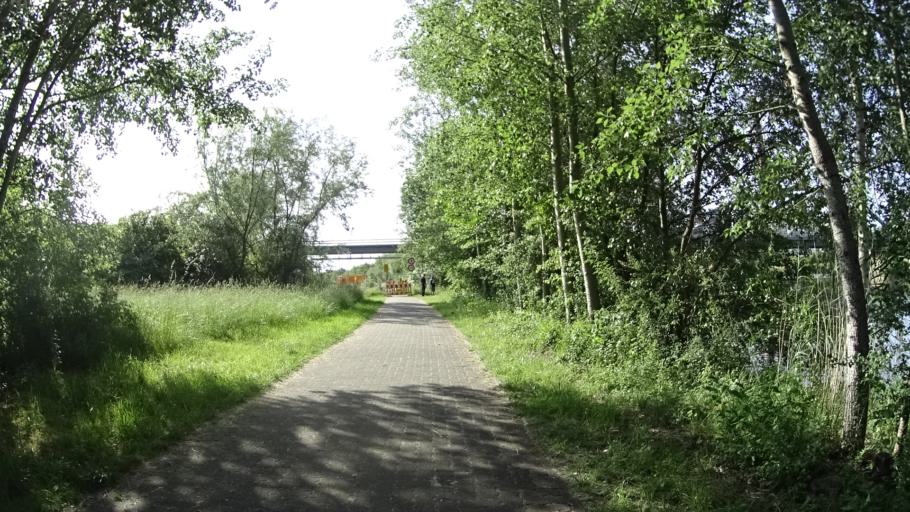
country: DE
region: Bavaria
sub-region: Regierungsbezirk Unterfranken
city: Stockstadt am Main
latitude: 49.9811
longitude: 9.0686
